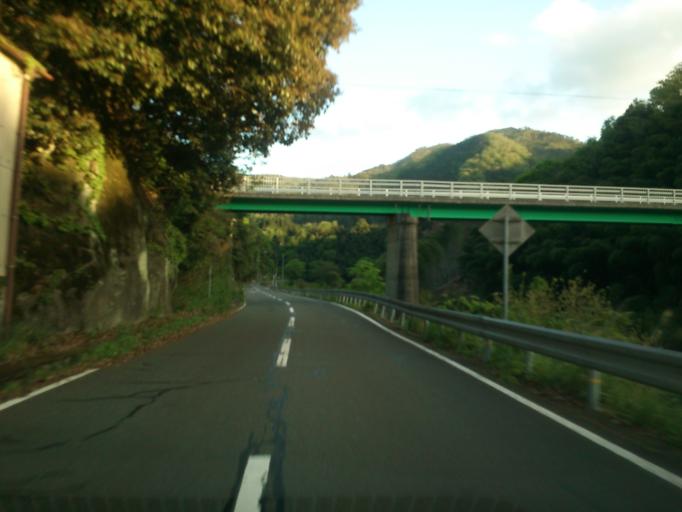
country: JP
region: Kyoto
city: Ayabe
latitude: 35.2747
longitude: 135.3639
